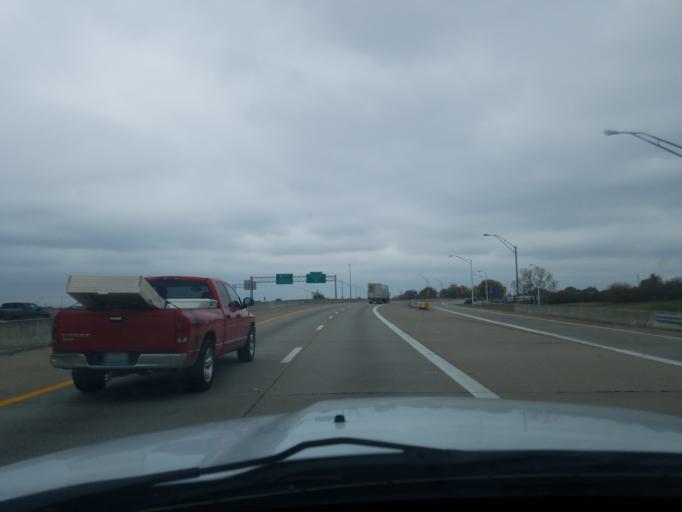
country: US
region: Kentucky
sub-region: Jefferson County
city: Audubon Park
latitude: 38.1883
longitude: -85.7272
